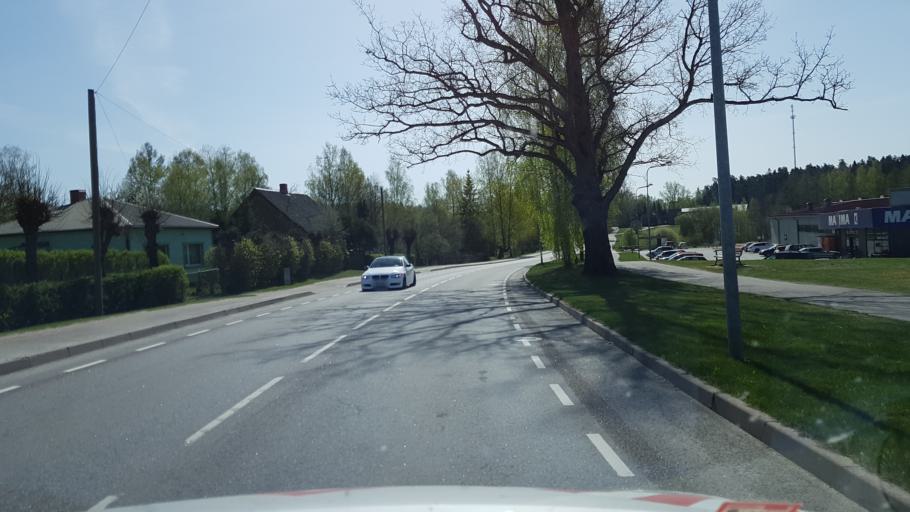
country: EE
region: Valgamaa
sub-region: Torva linn
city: Torva
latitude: 57.9987
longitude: 25.9323
